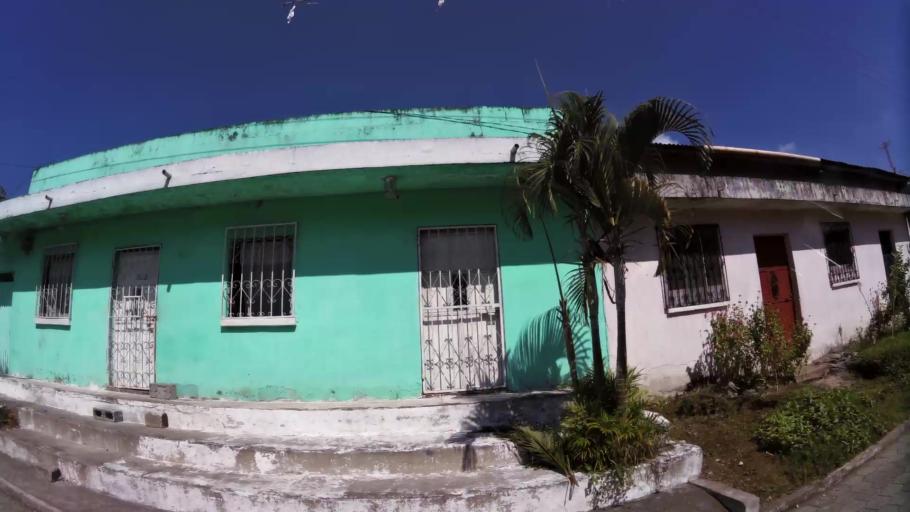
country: GT
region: Suchitepeque
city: Mazatenango
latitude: 14.5313
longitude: -91.4953
